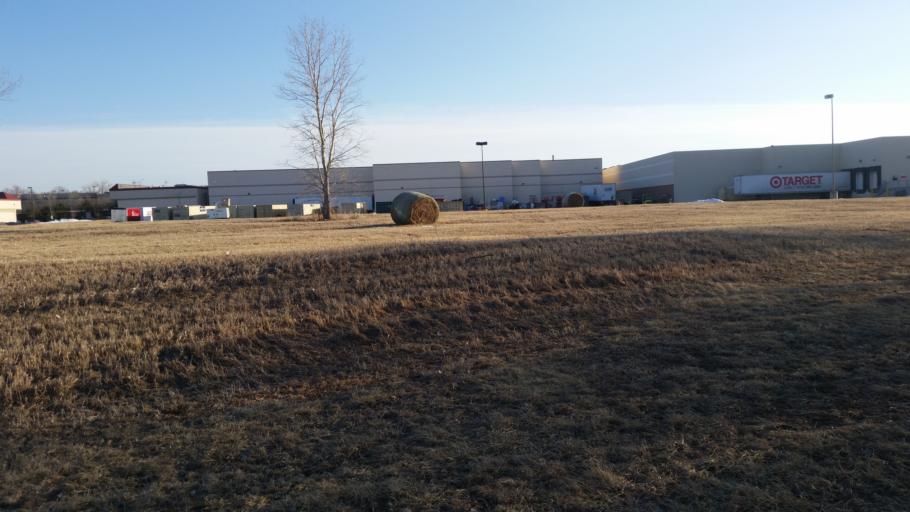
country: US
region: Nebraska
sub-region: Sarpy County
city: Offutt Air Force Base
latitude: 41.1440
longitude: -95.9690
